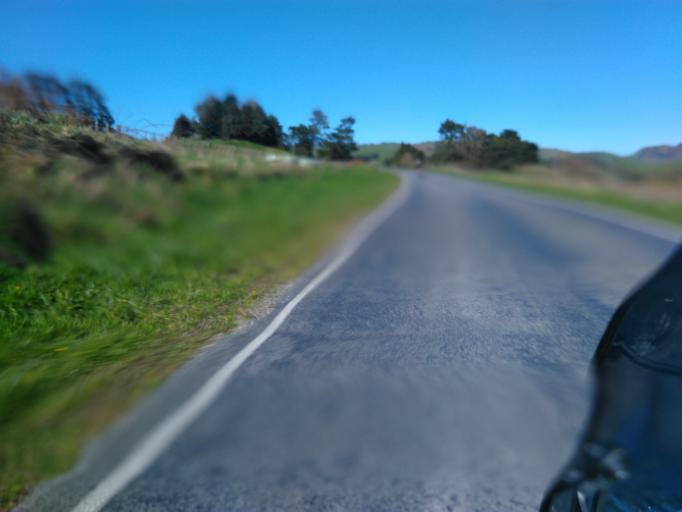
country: NZ
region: Bay of Plenty
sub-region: Opotiki District
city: Opotiki
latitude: -38.3450
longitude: 177.5331
